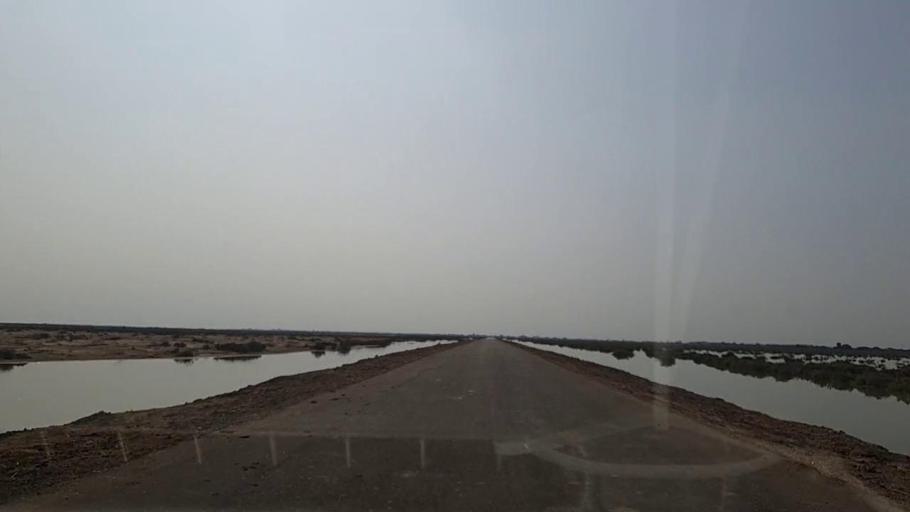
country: PK
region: Sindh
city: Chuhar Jamali
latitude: 24.2155
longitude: 67.8664
